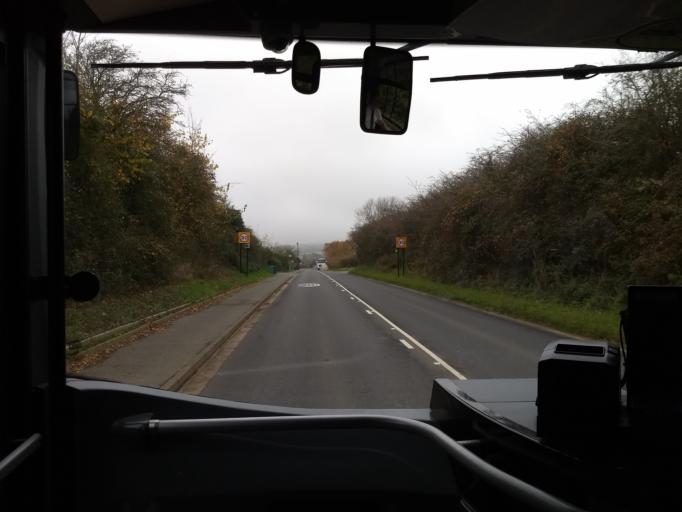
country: GB
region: England
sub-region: Isle of Wight
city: Newchurch
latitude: 50.6683
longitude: -1.2323
